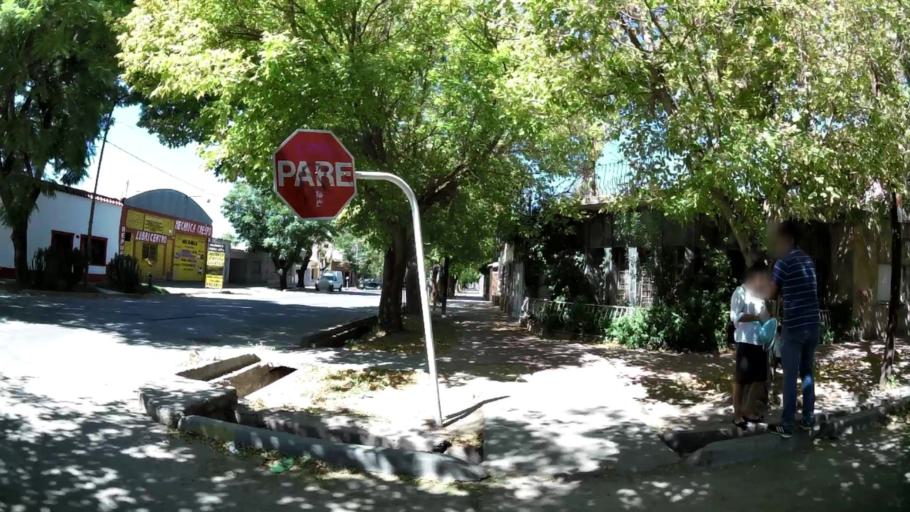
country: AR
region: Mendoza
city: Las Heras
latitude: -32.8518
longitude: -68.8333
